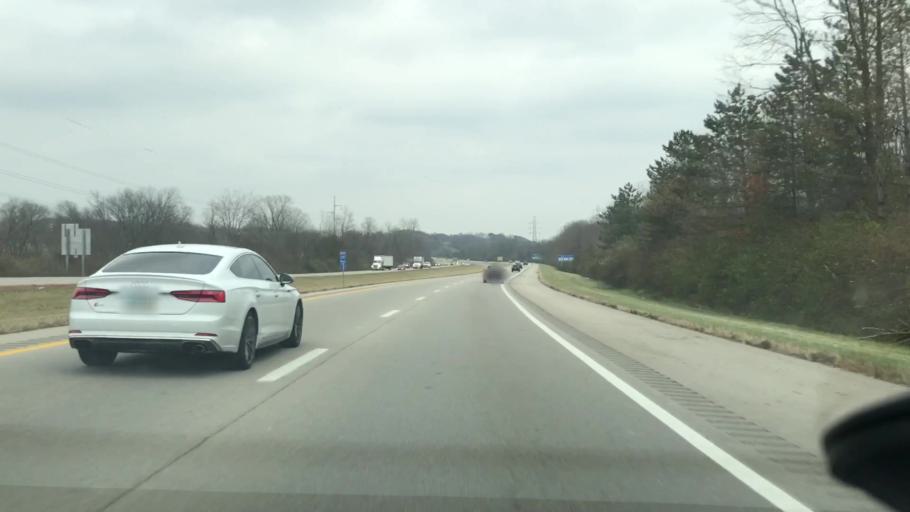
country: US
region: Ohio
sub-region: Greene County
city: Wright-Patterson AFB
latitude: 39.7762
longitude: -84.0346
